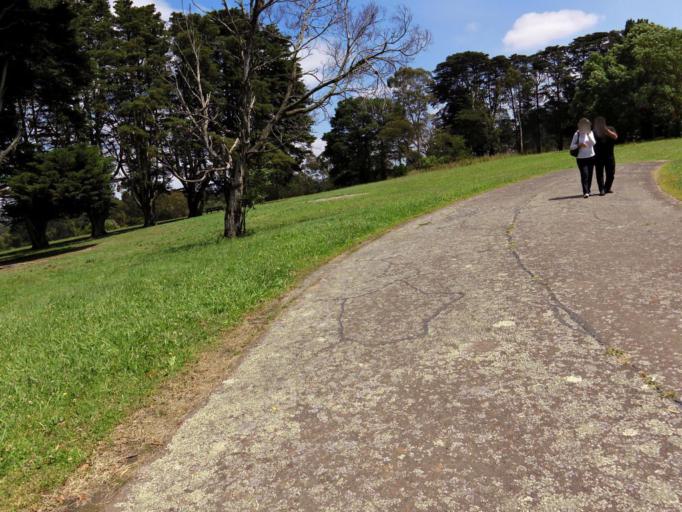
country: AU
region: Victoria
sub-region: Knox
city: Wantirna South
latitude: -37.8780
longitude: 145.1977
